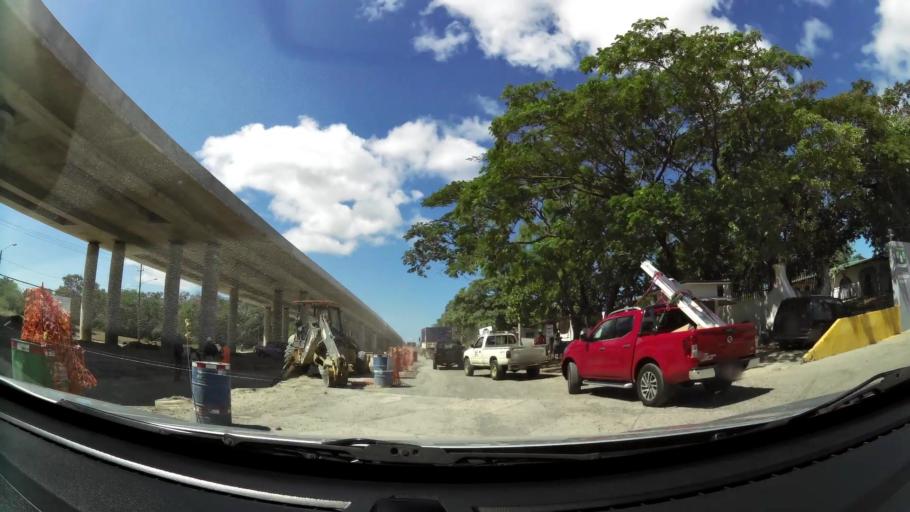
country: CR
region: Guanacaste
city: Bagaces
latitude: 10.5212
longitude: -85.2551
